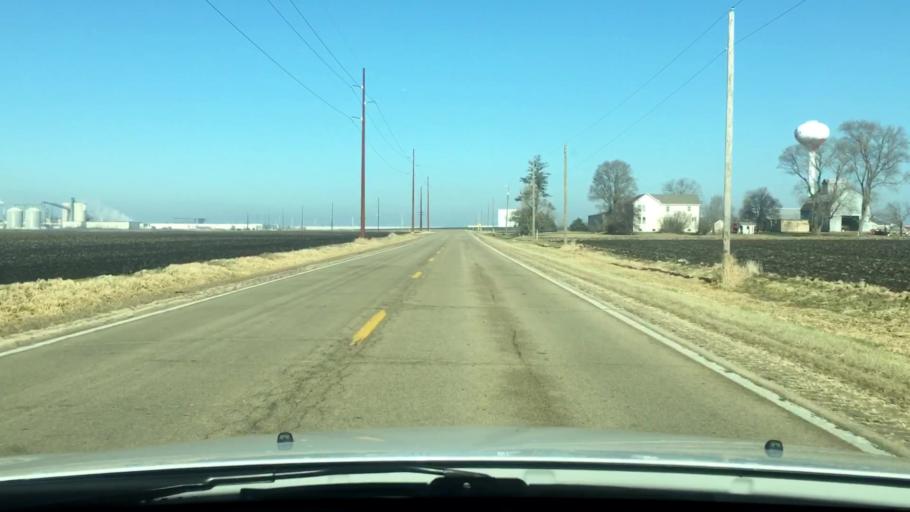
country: US
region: Illinois
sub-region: Ogle County
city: Rochelle
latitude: 41.8793
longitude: -89.0251
